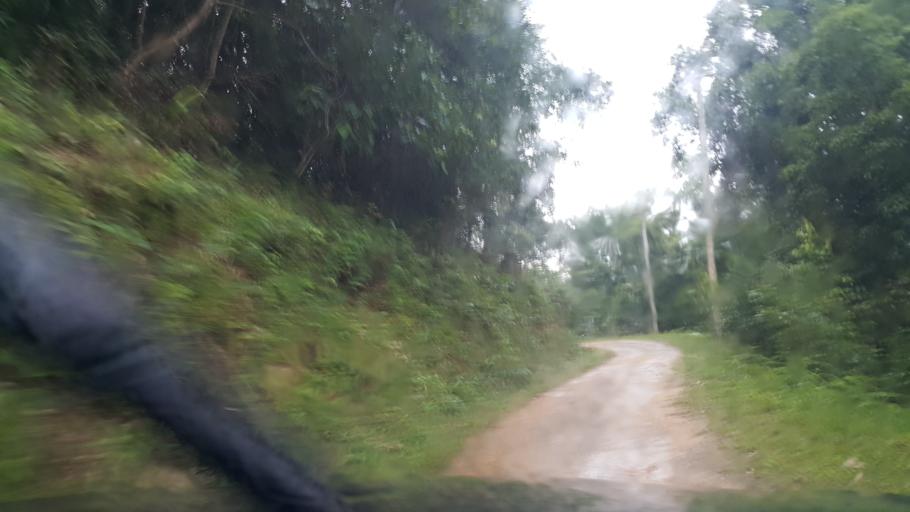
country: TH
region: Lampang
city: Wang Nuea
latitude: 19.1269
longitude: 99.3629
